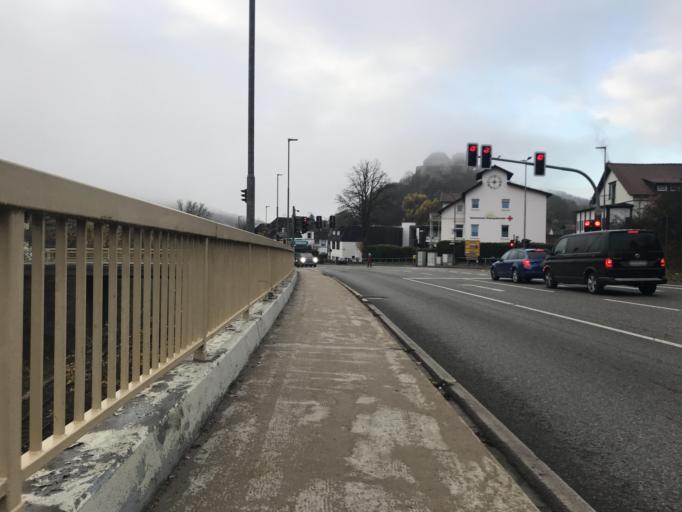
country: DE
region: Rheinland-Pfalz
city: Bad Munster am Stein-Ebernburg
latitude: 49.8108
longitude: 7.8428
